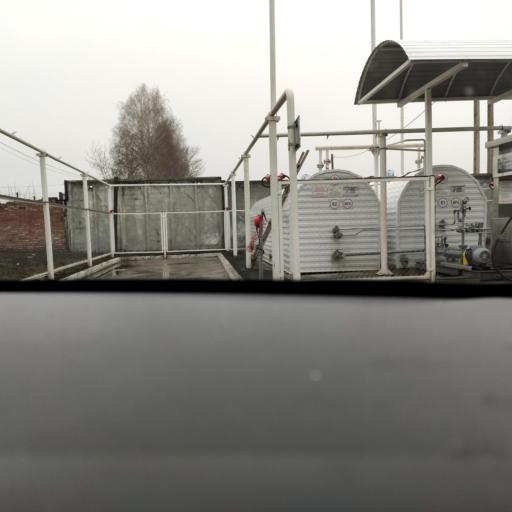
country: RU
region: Tatarstan
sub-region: Chistopol'skiy Rayon
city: Chistopol'
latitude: 55.3479
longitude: 50.6626
